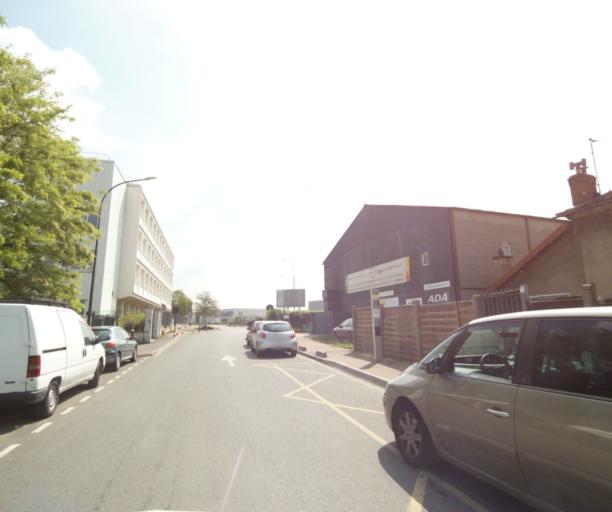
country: FR
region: Ile-de-France
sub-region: Departement des Yvelines
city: Sartrouville
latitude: 48.9471
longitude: 2.2110
